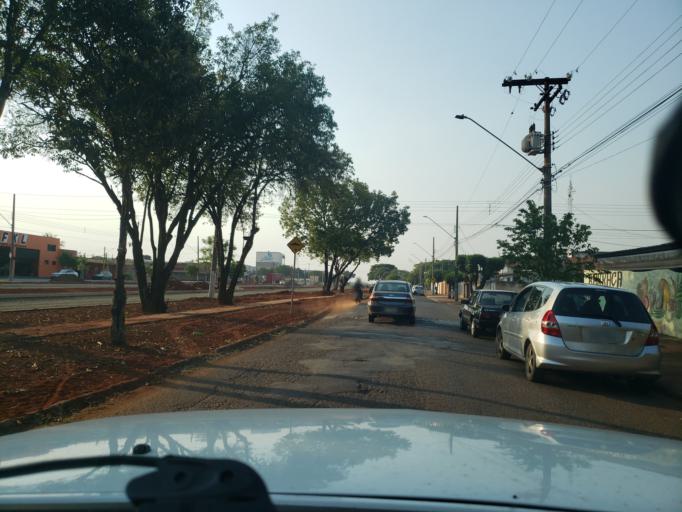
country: BR
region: Sao Paulo
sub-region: Moji-Guacu
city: Mogi-Gaucu
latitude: -22.3431
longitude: -46.9411
